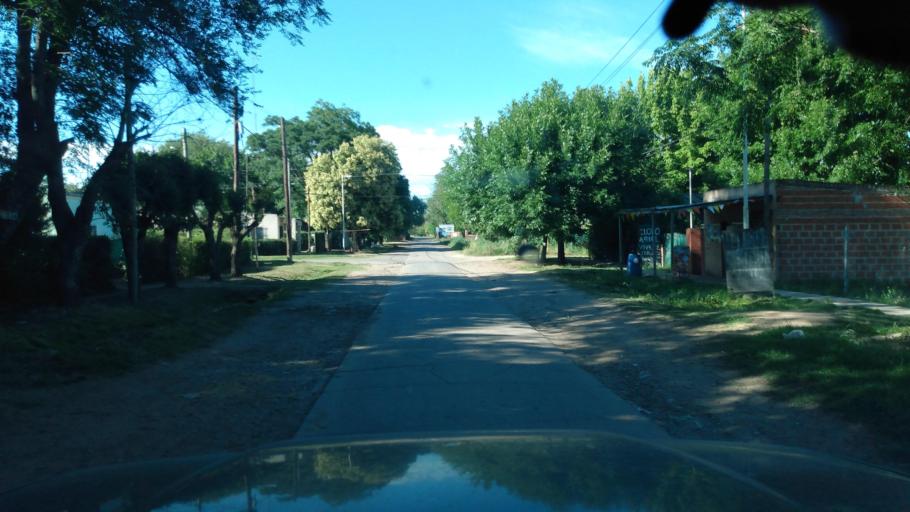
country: AR
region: Buenos Aires
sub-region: Partido de Lujan
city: Lujan
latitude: -34.5885
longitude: -59.0596
